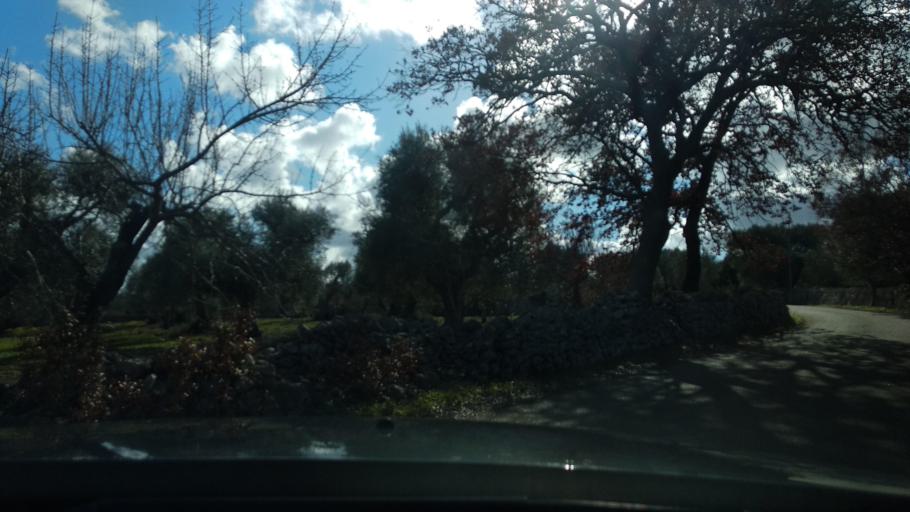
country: IT
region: Apulia
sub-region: Provincia di Brindisi
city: Casalini
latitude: 40.6934
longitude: 17.4868
